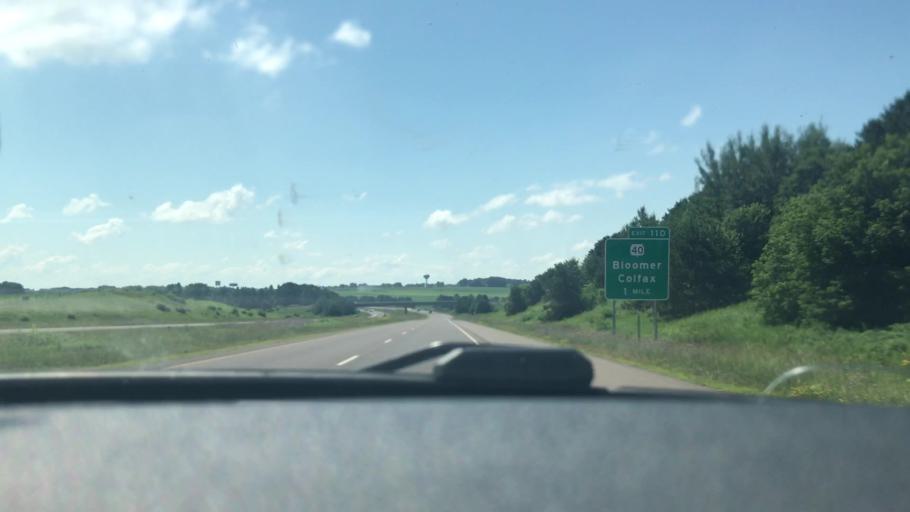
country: US
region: Wisconsin
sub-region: Chippewa County
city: Bloomer
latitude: 45.1158
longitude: -91.5193
